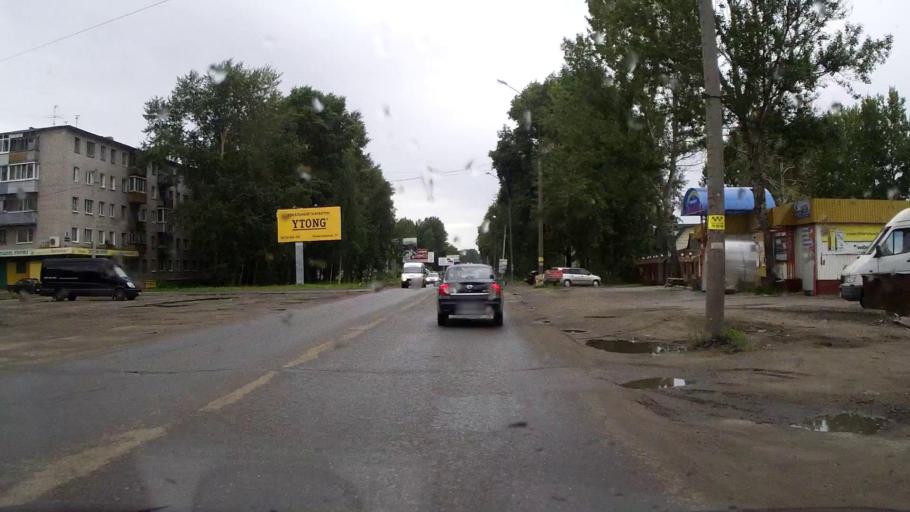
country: RU
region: Vologda
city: Vologda
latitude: 59.2065
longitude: 39.8626
